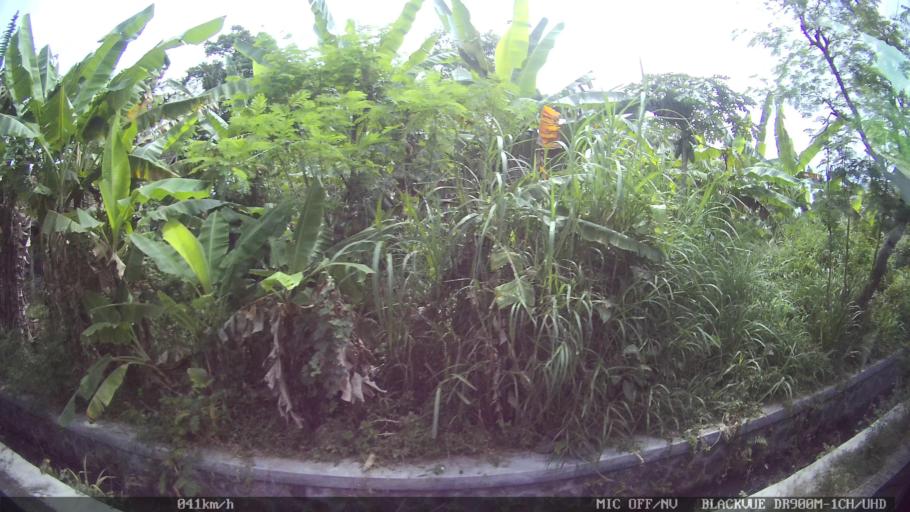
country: ID
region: Central Java
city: Candi Prambanan
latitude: -7.7435
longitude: 110.4813
